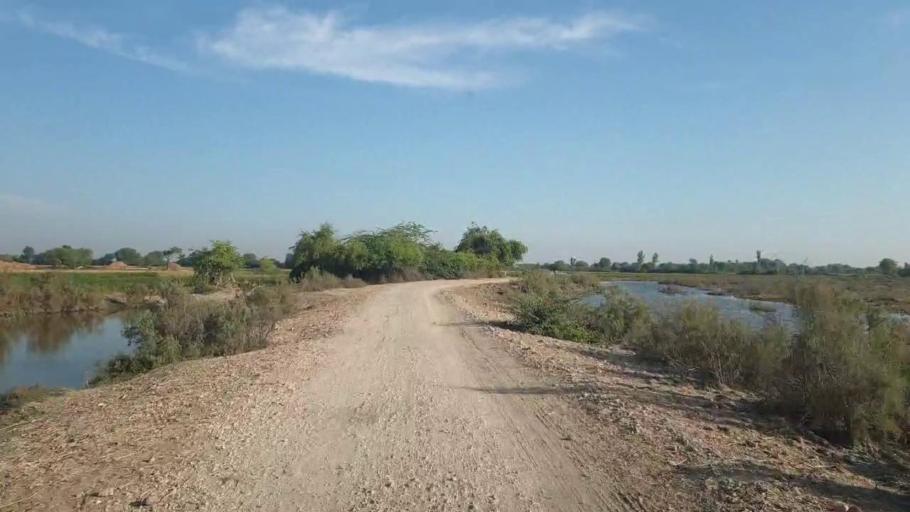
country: PK
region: Sindh
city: Talhar
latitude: 24.8212
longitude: 68.8387
